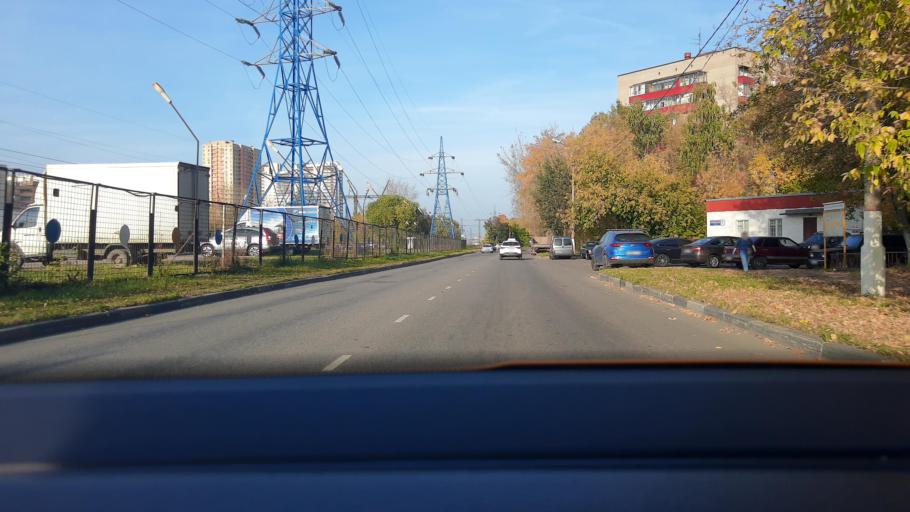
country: RU
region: Moskovskaya
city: Reutov
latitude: 55.7638
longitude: 37.8498
